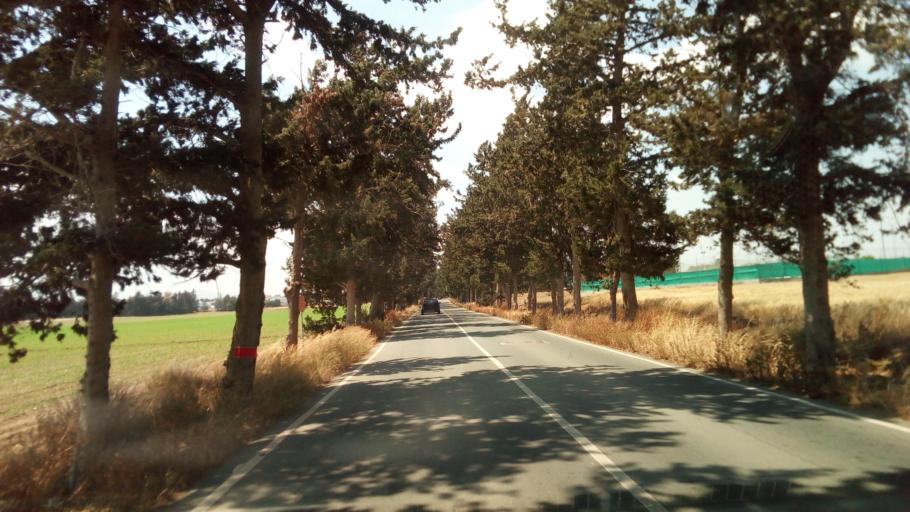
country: CY
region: Larnaka
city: Meneou
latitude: 34.8537
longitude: 33.6051
